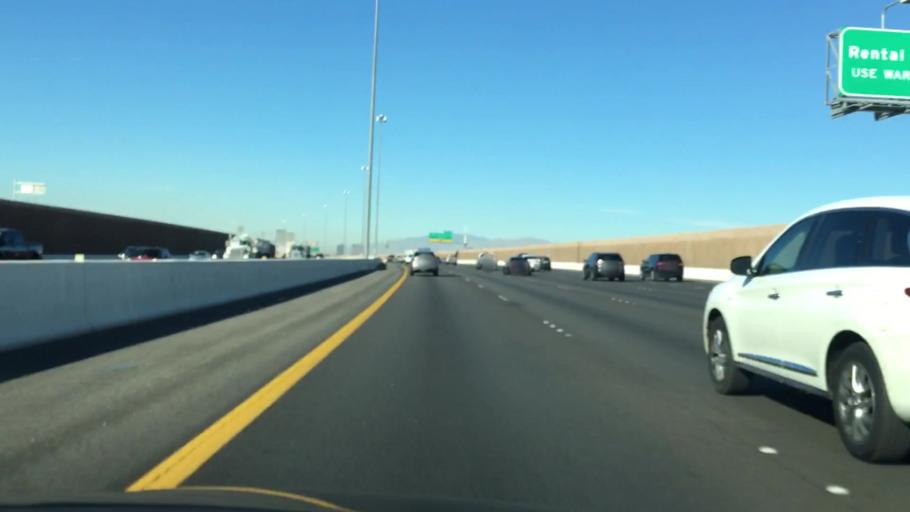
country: US
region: Nevada
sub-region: Clark County
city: Paradise
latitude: 36.0469
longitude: -115.1345
